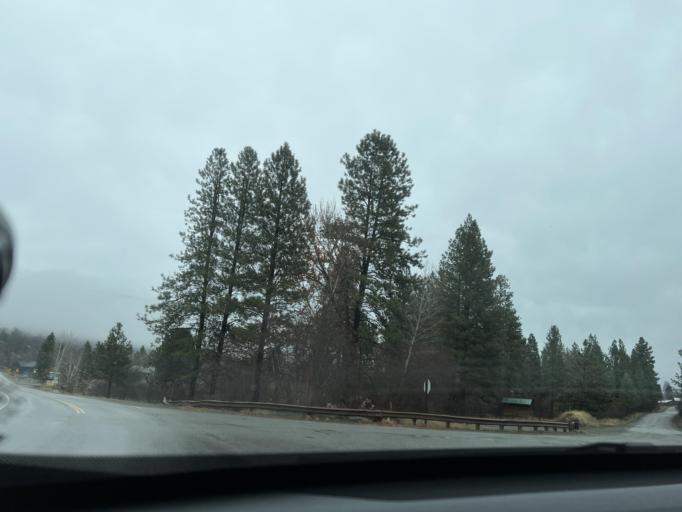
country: US
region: Washington
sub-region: Okanogan County
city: Brewster
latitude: 48.4712
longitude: -120.1843
